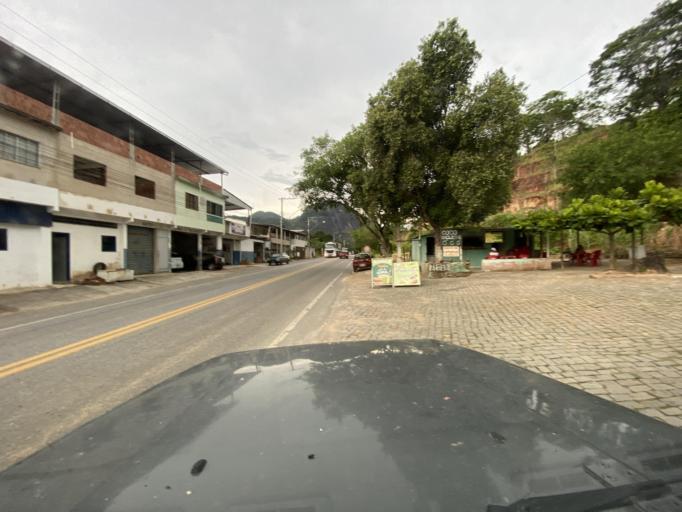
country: BR
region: Espirito Santo
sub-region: Jeronimo Monteiro
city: Jeronimo Monteiro
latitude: -20.7909
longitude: -41.3881
